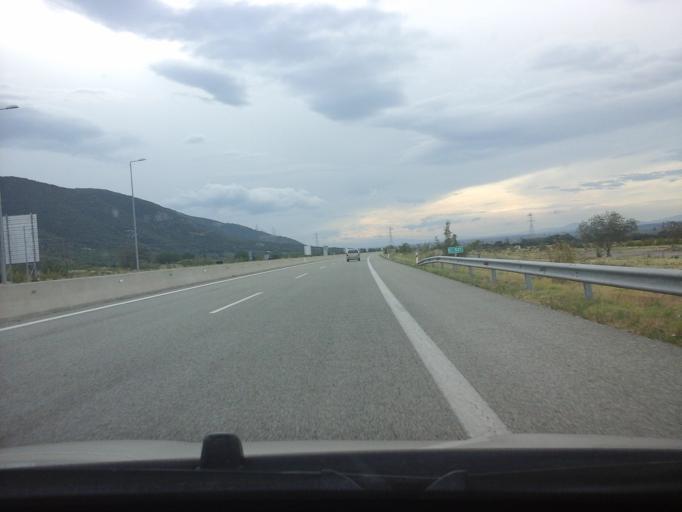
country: GR
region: East Macedonia and Thrace
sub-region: Nomos Xanthis
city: Selero
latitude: 41.1203
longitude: 25.0813
